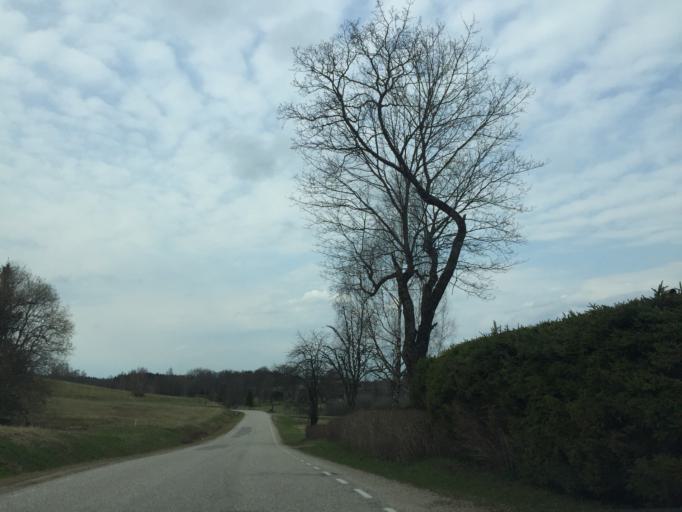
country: EE
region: Vorumaa
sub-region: Voru linn
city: Voru
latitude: 57.7152
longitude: 27.0551
